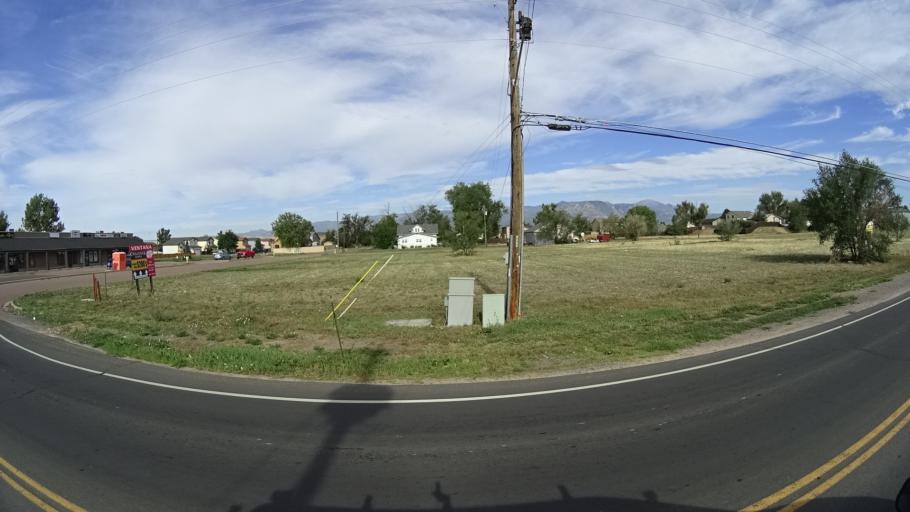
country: US
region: Colorado
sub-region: El Paso County
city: Fountain
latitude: 38.6941
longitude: -104.6968
